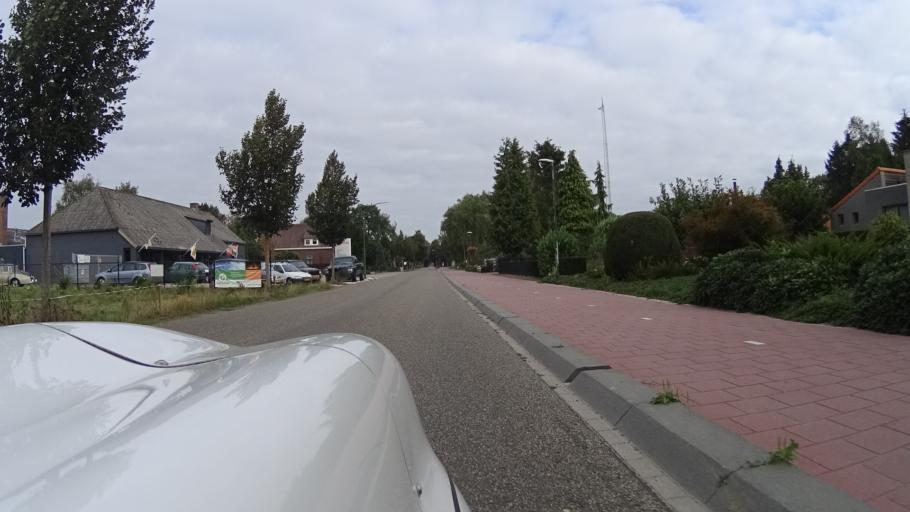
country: NL
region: North Brabant
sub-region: Gemeente Boxmeer
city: Overloon
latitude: 51.5991
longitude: 5.9196
